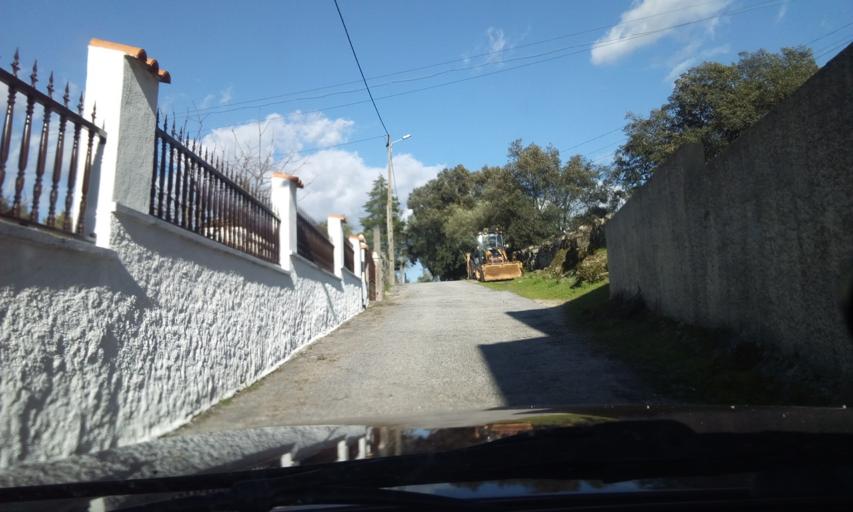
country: PT
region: Guarda
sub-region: Fornos de Algodres
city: Fornos de Algodres
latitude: 40.6105
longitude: -7.5054
